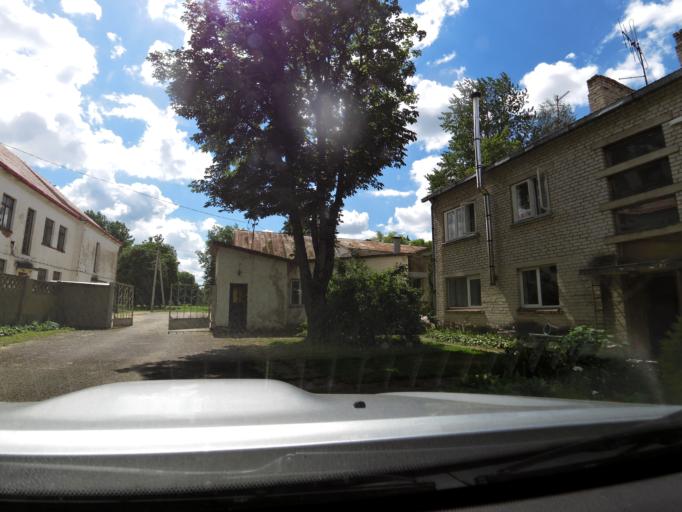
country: LT
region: Vilnius County
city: Elektrenai
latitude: 54.9530
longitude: 24.6550
